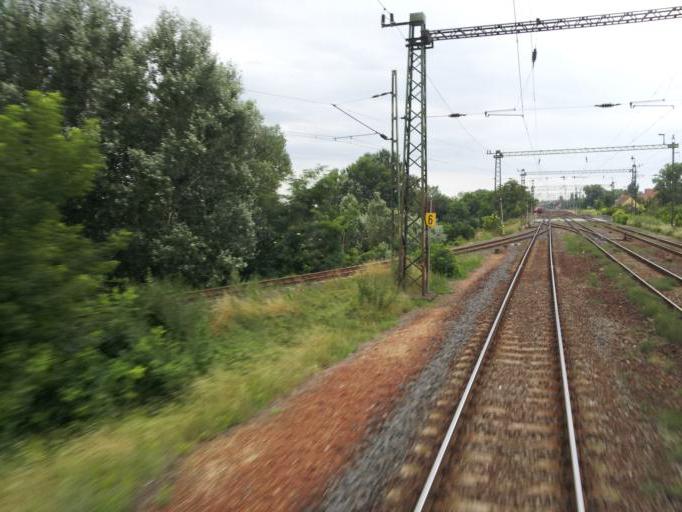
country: HU
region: Fejer
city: Szabadbattyan
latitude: 47.1091
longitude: 18.3958
